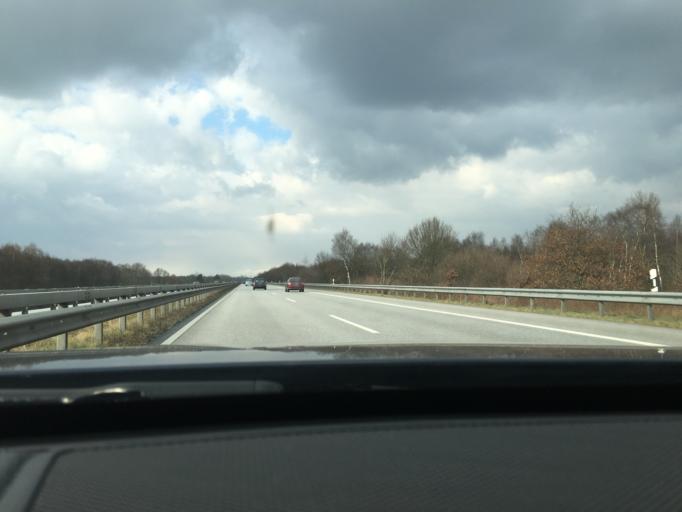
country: DE
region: Lower Saxony
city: Uthlede
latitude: 53.3493
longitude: 8.5977
